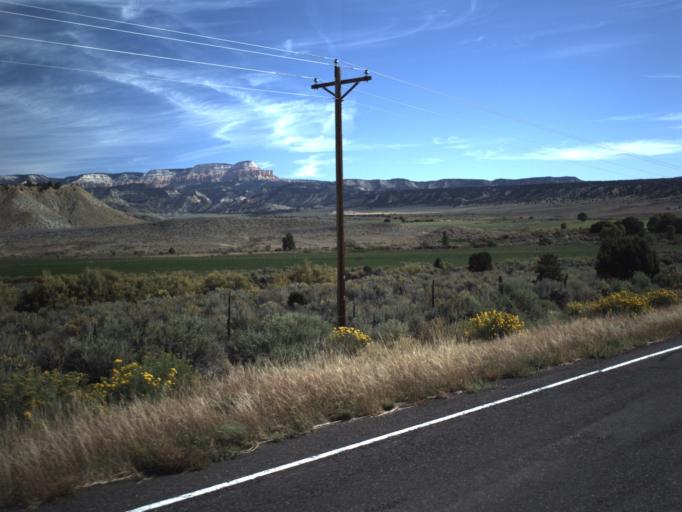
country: US
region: Utah
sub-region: Garfield County
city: Panguitch
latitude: 37.6133
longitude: -112.0693
